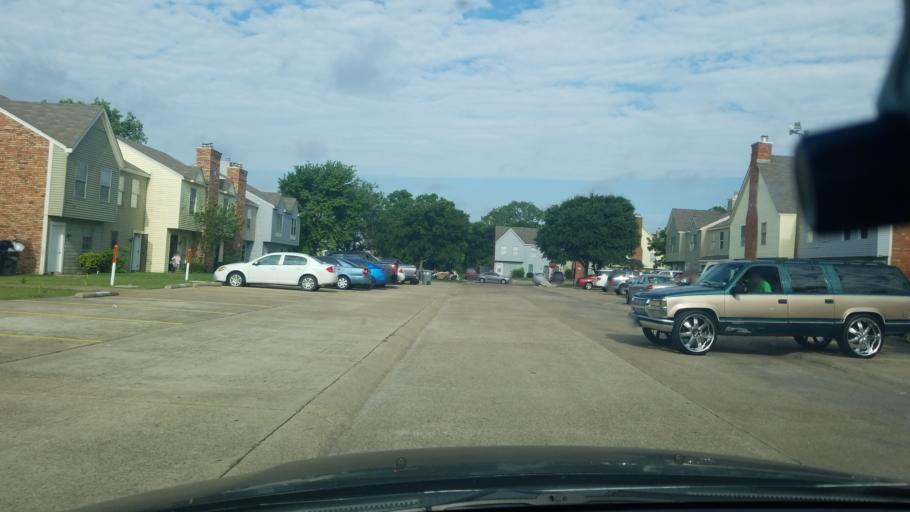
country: US
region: Texas
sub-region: Dallas County
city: Balch Springs
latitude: 32.7515
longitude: -96.6591
